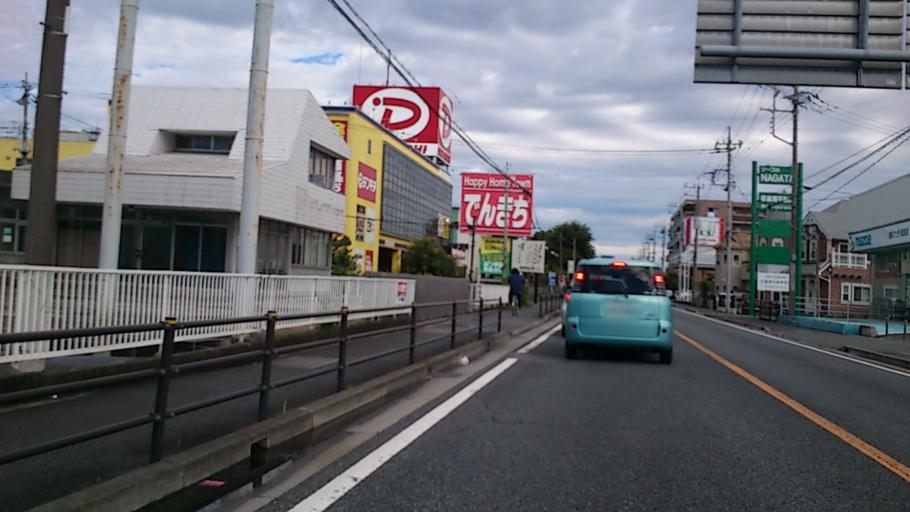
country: JP
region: Saitama
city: Kumagaya
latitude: 36.1735
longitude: 139.3407
